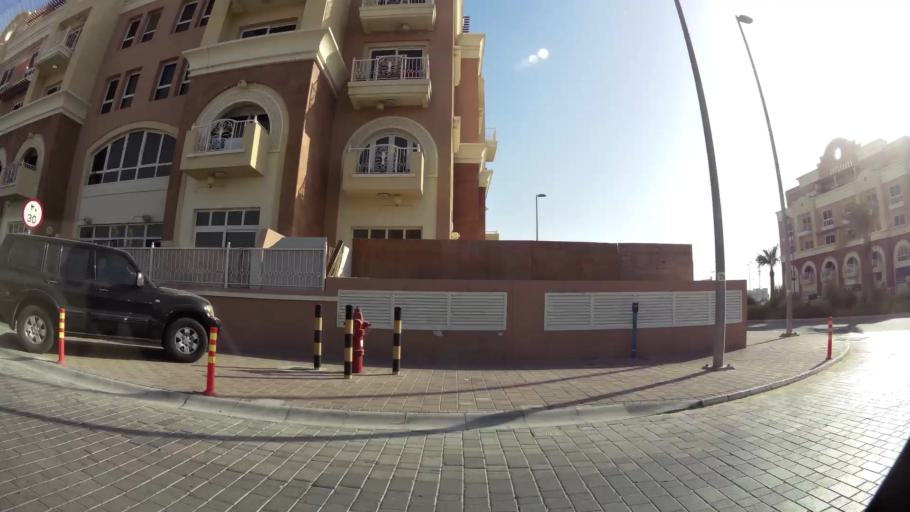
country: AE
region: Dubai
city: Dubai
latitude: 25.0526
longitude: 55.2150
